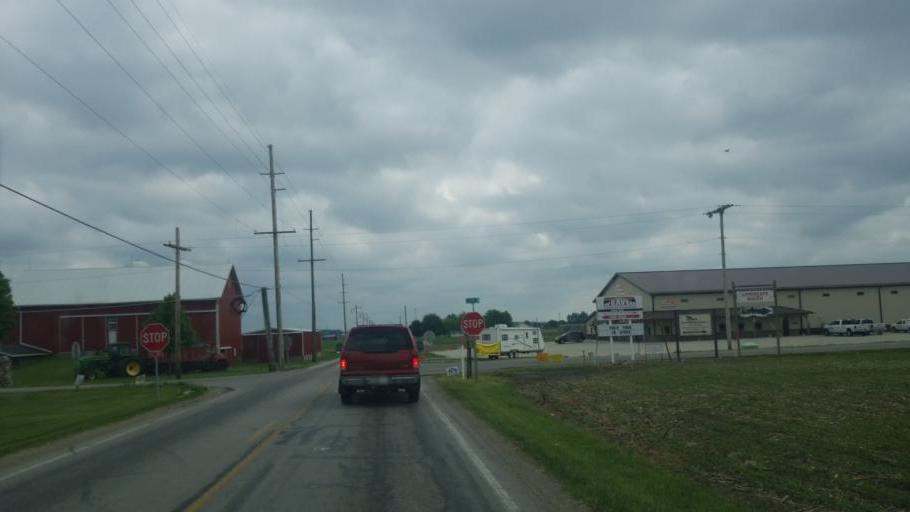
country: US
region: Indiana
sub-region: Elkhart County
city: Nappanee
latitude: 41.4271
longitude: -86.0013
